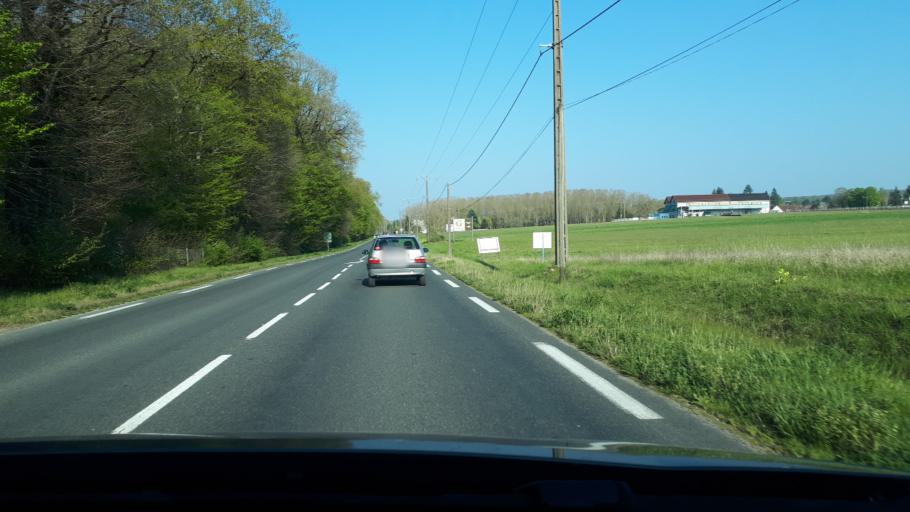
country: FR
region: Centre
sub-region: Departement d'Indre-et-Loire
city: Civray-de-Touraine
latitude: 47.3212
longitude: 1.0730
